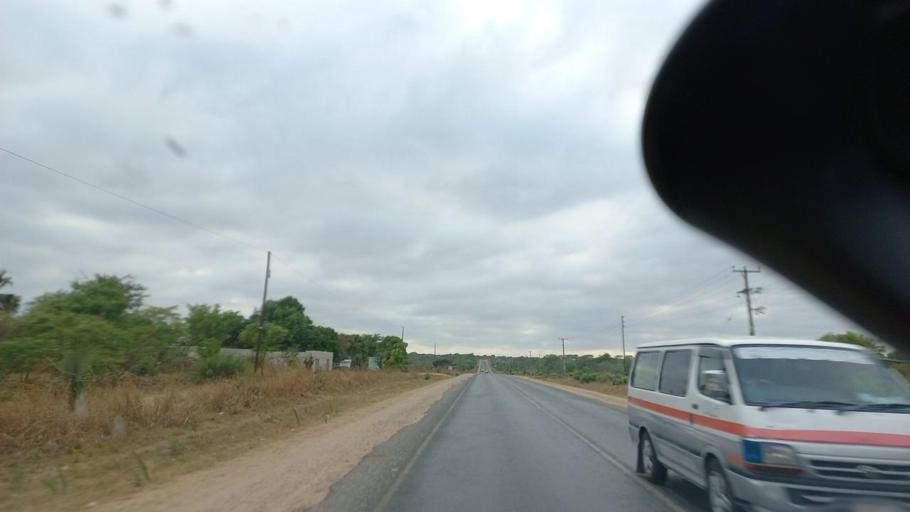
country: ZM
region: Lusaka
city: Chongwe
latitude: -15.3405
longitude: 28.6250
